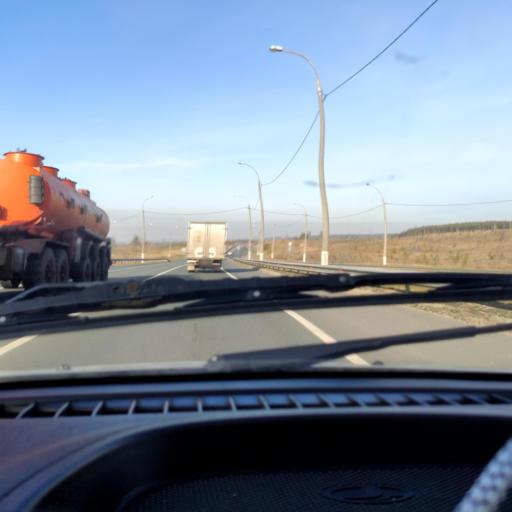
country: RU
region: Samara
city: Zhigulevsk
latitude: 53.5019
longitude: 49.5390
